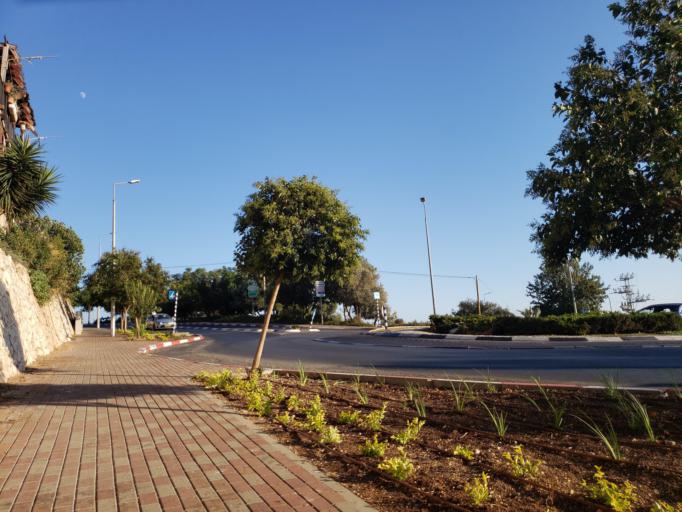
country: IL
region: Northern District
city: Safed
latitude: 32.9580
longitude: 35.4913
